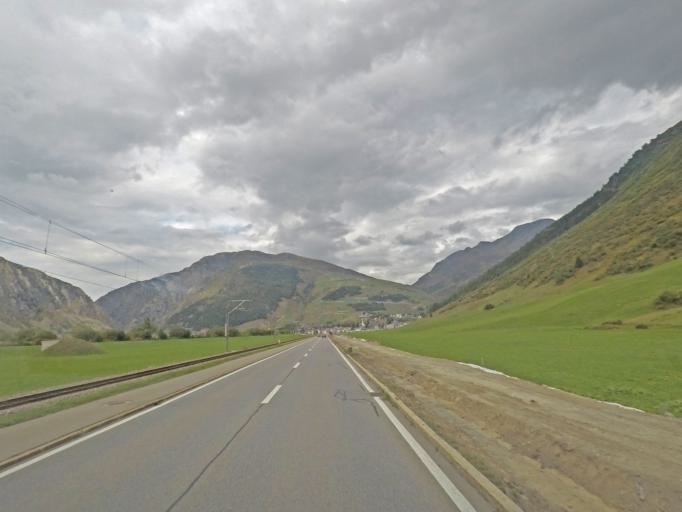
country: CH
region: Uri
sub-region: Uri
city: Andermatt
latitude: 46.6272
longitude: 8.5818
